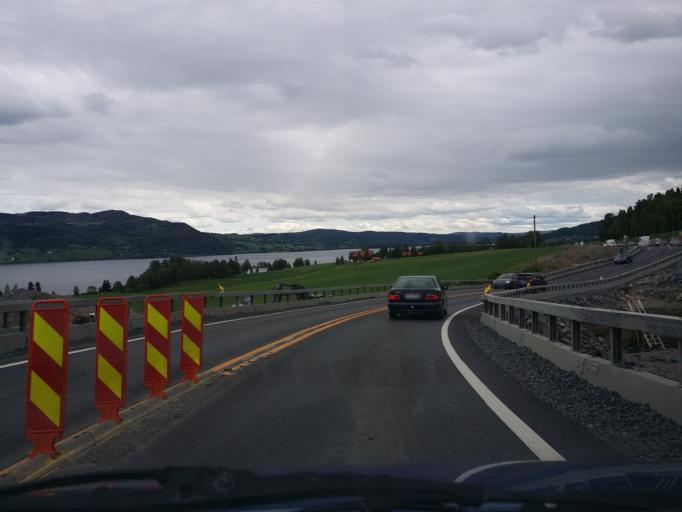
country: NO
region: Hedmark
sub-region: Ringsaker
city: Moelv
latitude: 60.9783
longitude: 10.5826
